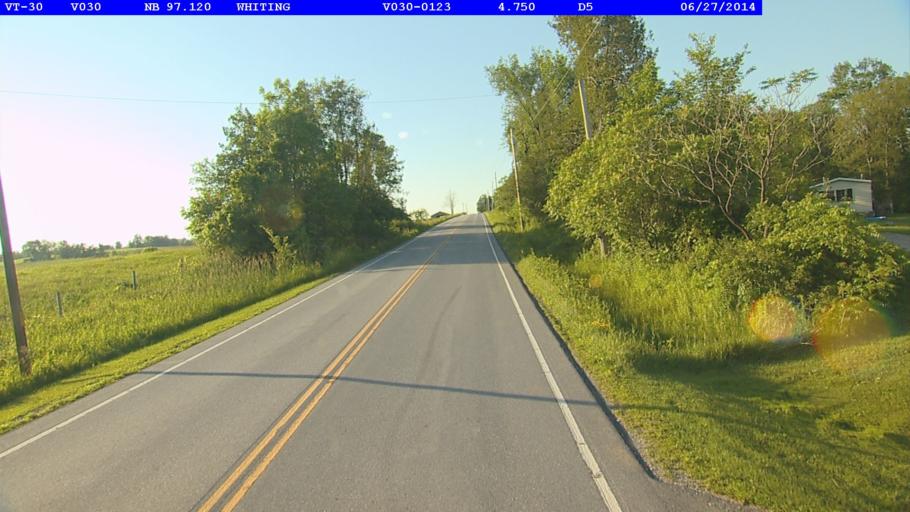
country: US
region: Vermont
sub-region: Addison County
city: Middlebury (village)
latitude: 43.9053
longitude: -73.2079
